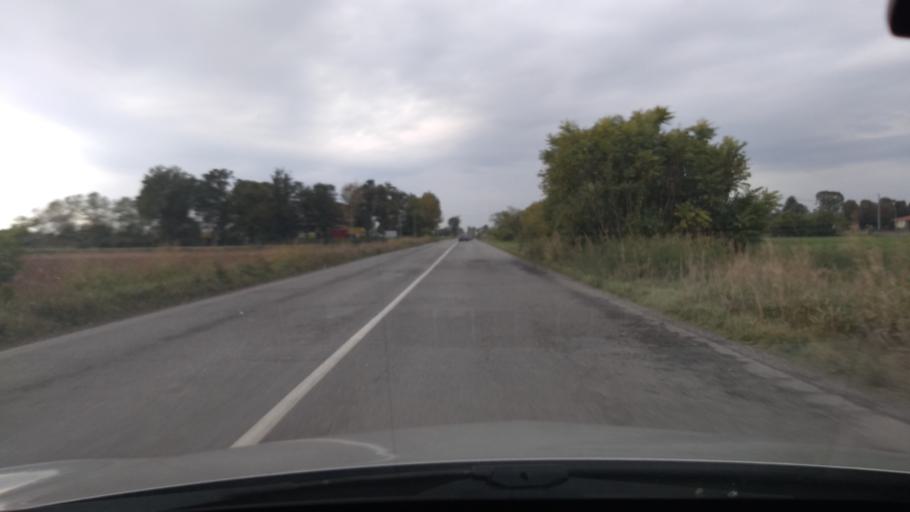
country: IT
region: Lombardy
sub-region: Provincia di Bergamo
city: Urgnano
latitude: 45.5910
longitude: 9.6952
